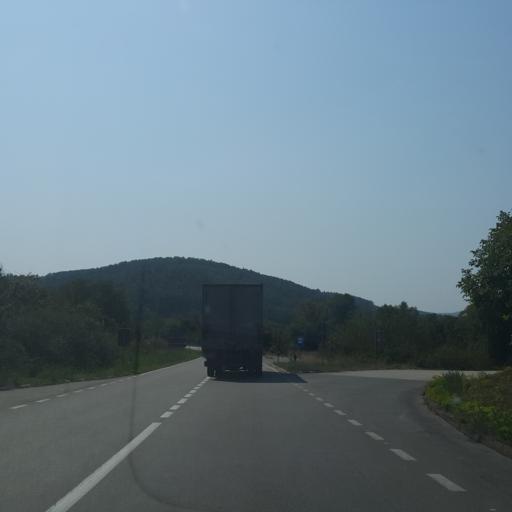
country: RS
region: Central Serbia
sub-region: Zajecarski Okrug
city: Zajecar
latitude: 43.8175
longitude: 22.2867
